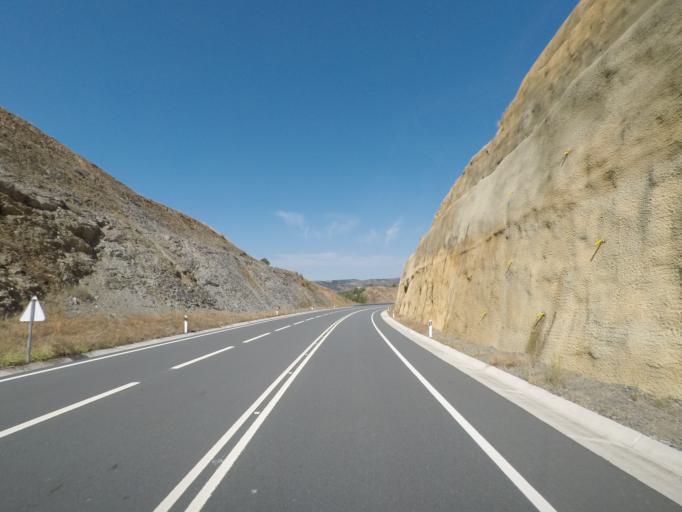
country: PT
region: Braganca
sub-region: Alfandega da Fe
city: Alfandega da Fe
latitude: 41.2965
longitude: -6.8983
